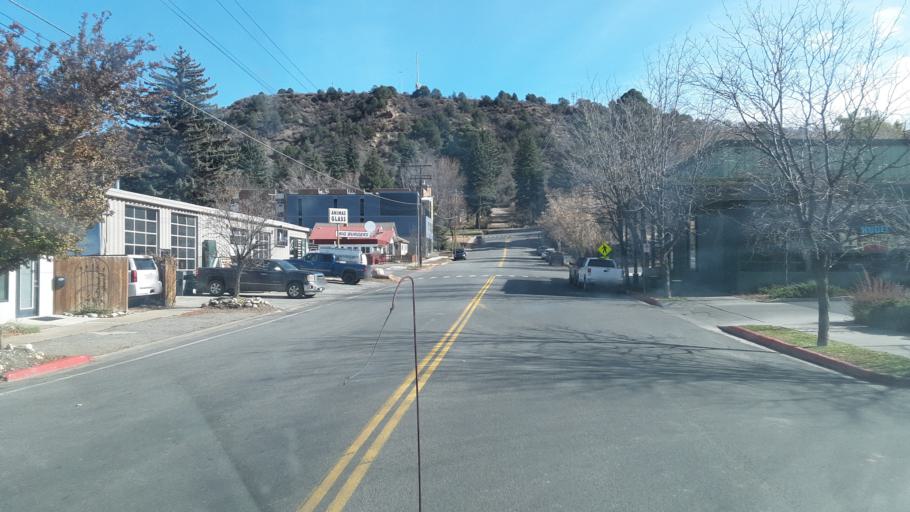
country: US
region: Colorado
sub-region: La Plata County
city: Durango
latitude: 37.2785
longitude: -107.8784
